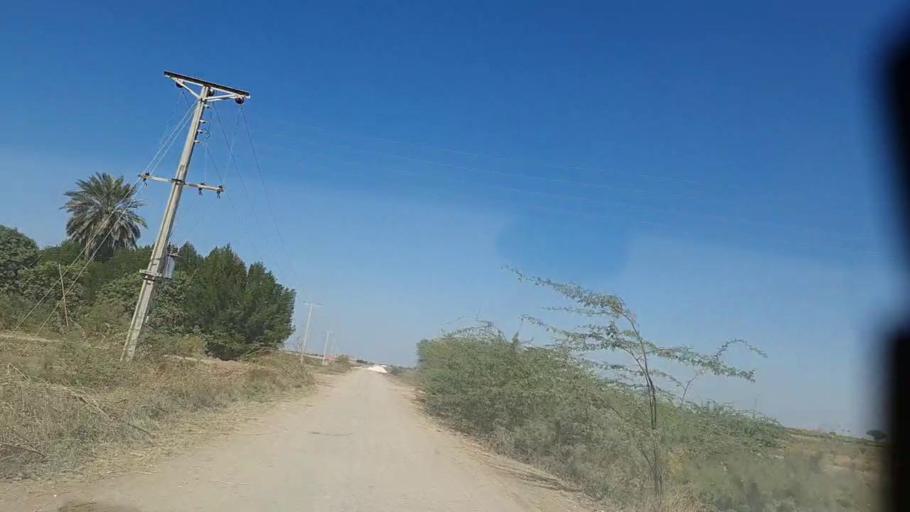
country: PK
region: Sindh
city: Digri
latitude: 25.1527
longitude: 69.0487
